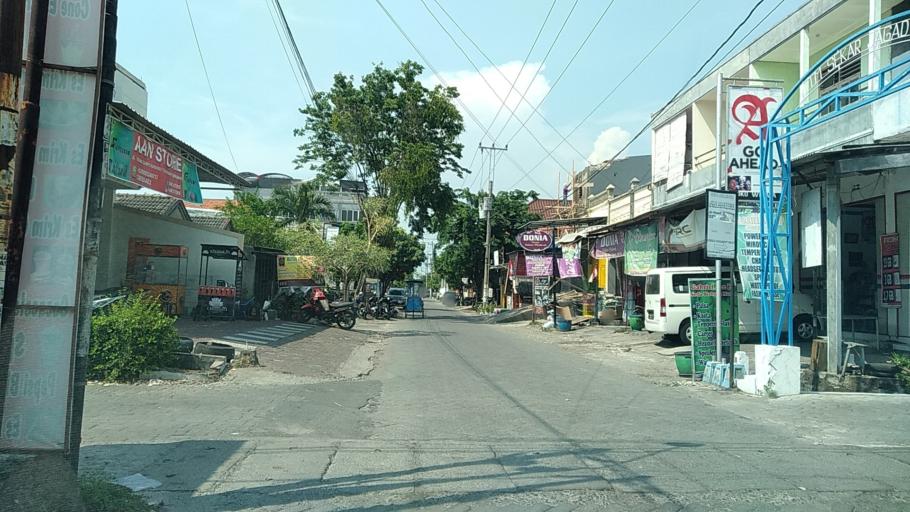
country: ID
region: Central Java
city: Semarang
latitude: -6.9818
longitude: 110.4608
